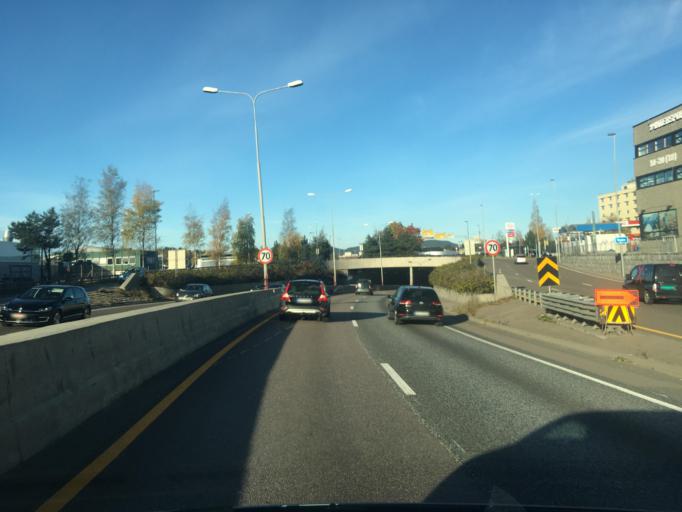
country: NO
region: Oslo
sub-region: Oslo
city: Oslo
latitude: 59.8932
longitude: 10.8041
